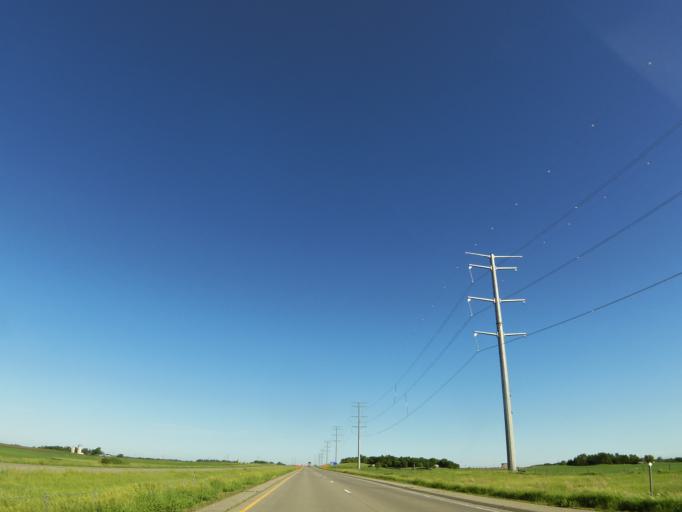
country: US
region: Minnesota
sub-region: Douglas County
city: Osakis
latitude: 45.8199
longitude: -95.1258
